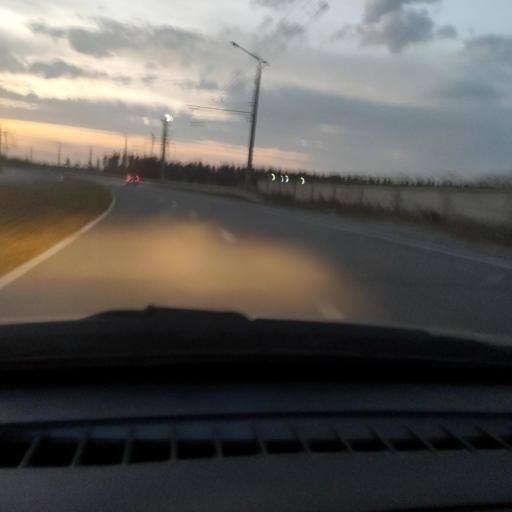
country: RU
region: Samara
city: Povolzhskiy
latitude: 53.5482
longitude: 49.5999
